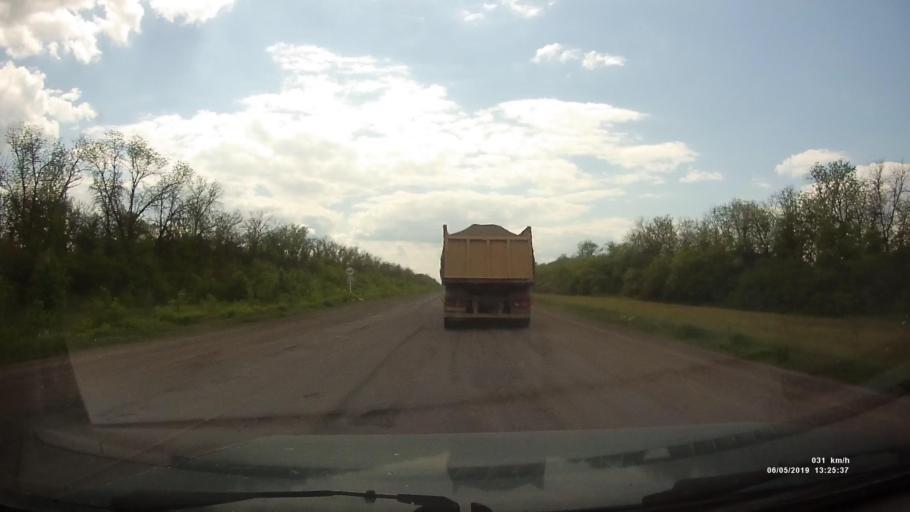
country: RU
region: Rostov
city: Ust'-Donetskiy
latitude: 47.6820
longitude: 40.9035
